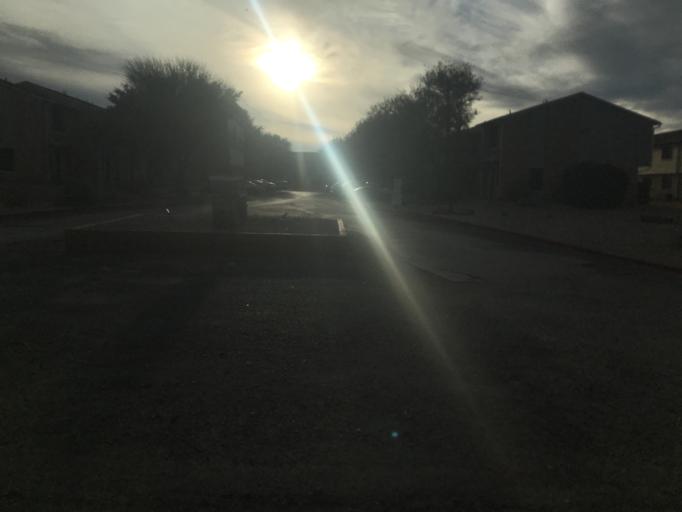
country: US
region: Texas
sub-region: Taylor County
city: Abilene
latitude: 32.4201
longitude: -99.7829
